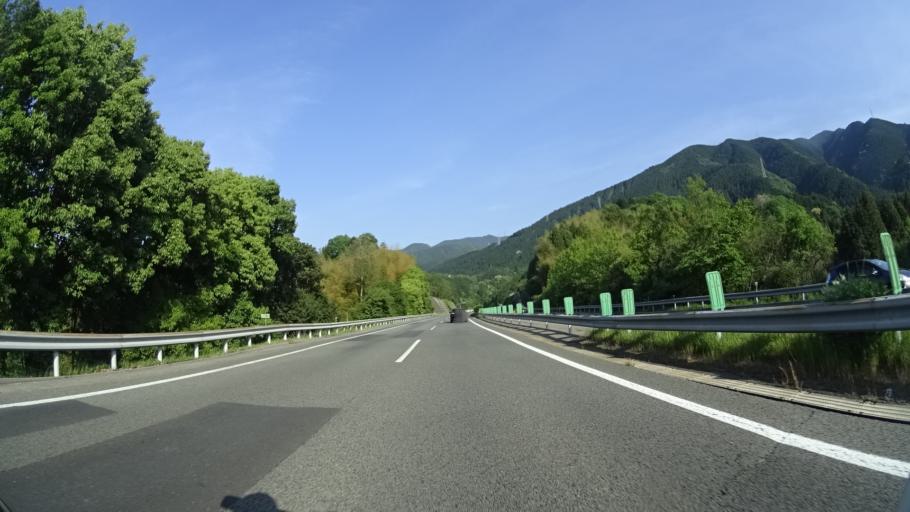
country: JP
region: Ehime
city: Saijo
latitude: 33.9111
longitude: 133.2461
